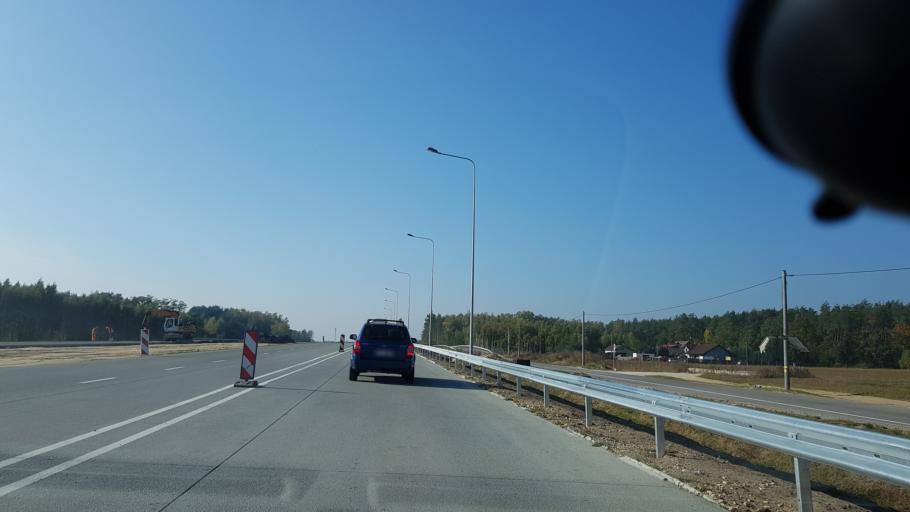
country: PL
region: Lodz Voivodeship
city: Zabia Wola
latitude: 52.0497
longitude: 20.7144
